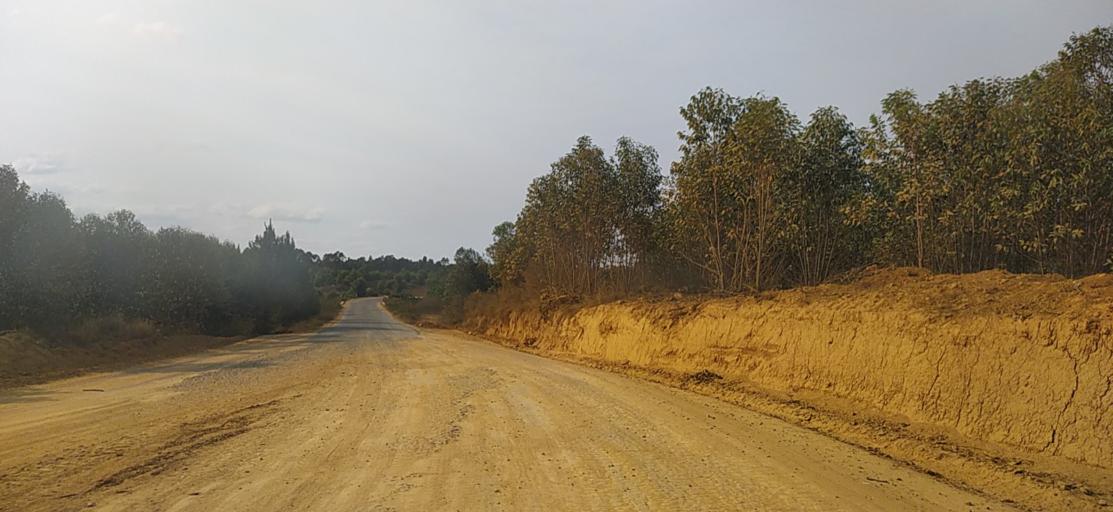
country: MG
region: Alaotra Mangoro
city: Moramanga
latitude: -18.6541
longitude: 48.2745
